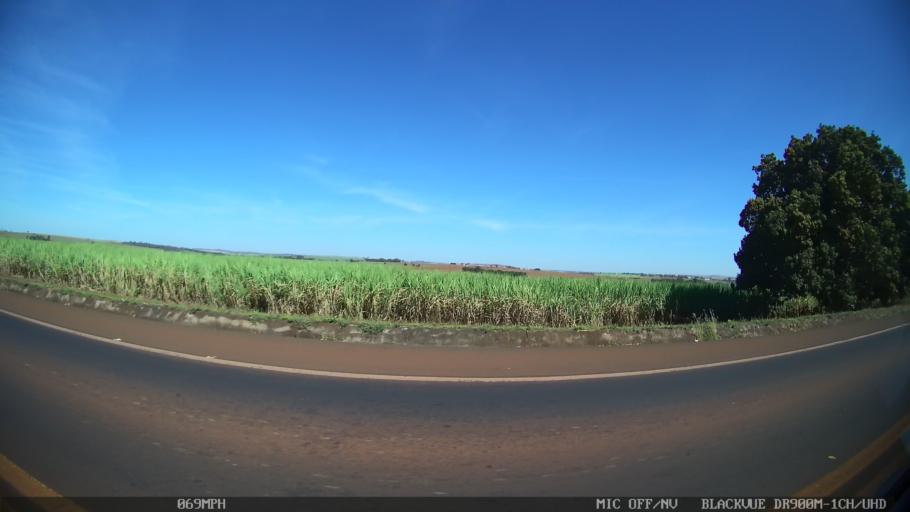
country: BR
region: Sao Paulo
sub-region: Sao Joaquim Da Barra
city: Sao Joaquim da Barra
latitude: -20.5374
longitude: -47.8243
